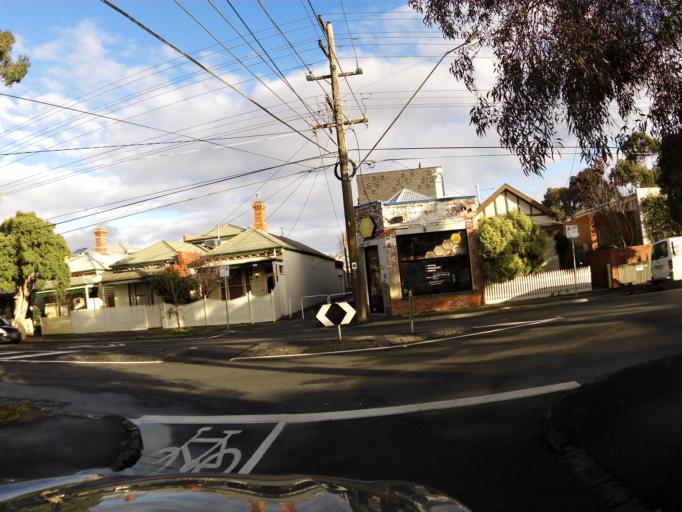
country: AU
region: Victoria
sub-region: Yarra
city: Richmond
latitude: -37.8140
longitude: 145.0047
